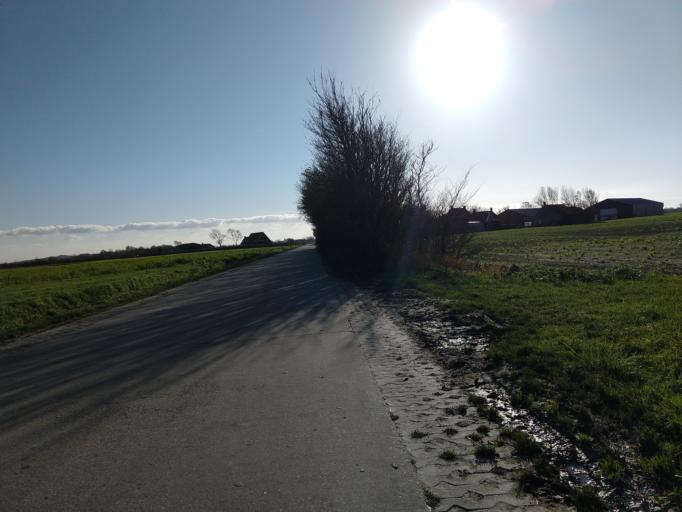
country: NL
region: Zeeland
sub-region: Gemeente Vlissingen
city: Vlissingen
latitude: 51.5330
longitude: 3.4800
